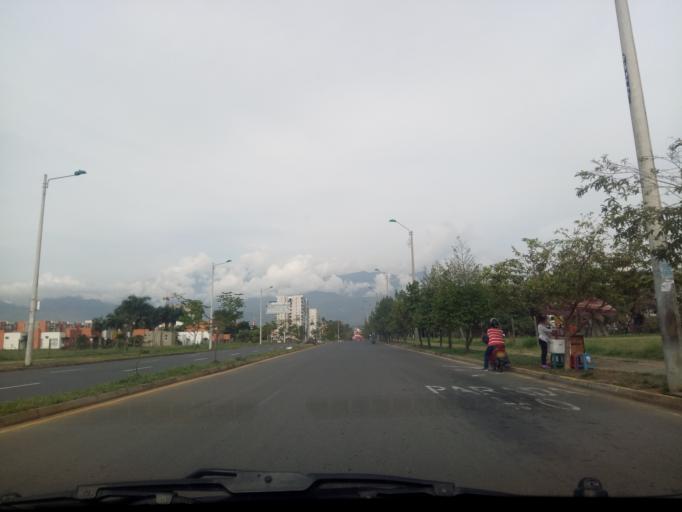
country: CO
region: Valle del Cauca
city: Cali
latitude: 3.3684
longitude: -76.5120
